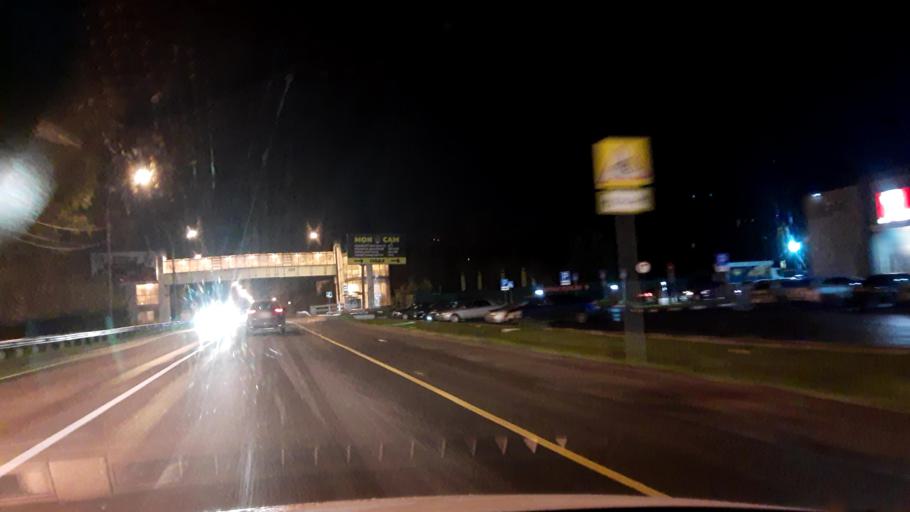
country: RU
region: Moskovskaya
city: Elektrostal'
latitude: 55.8052
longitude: 38.4278
